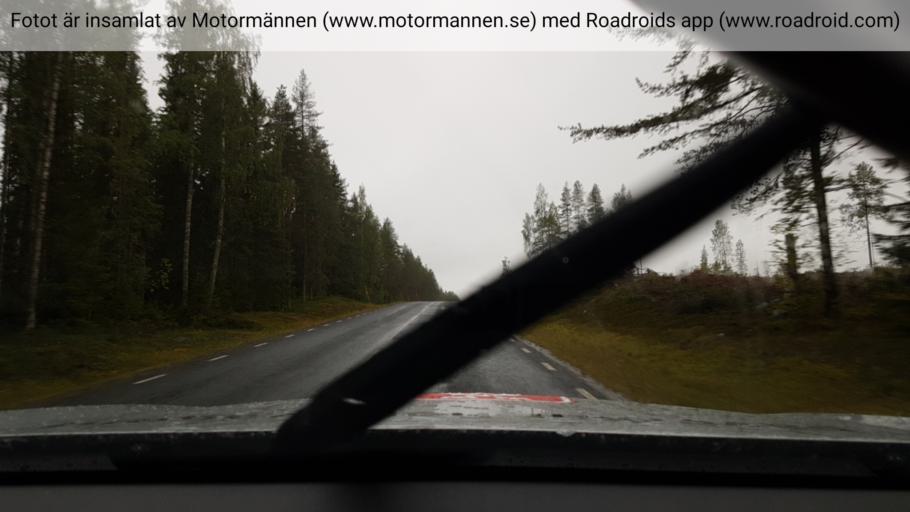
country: SE
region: Vaesterbotten
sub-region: Skelleftea Kommun
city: Storvik
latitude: 64.9668
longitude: 20.6673
